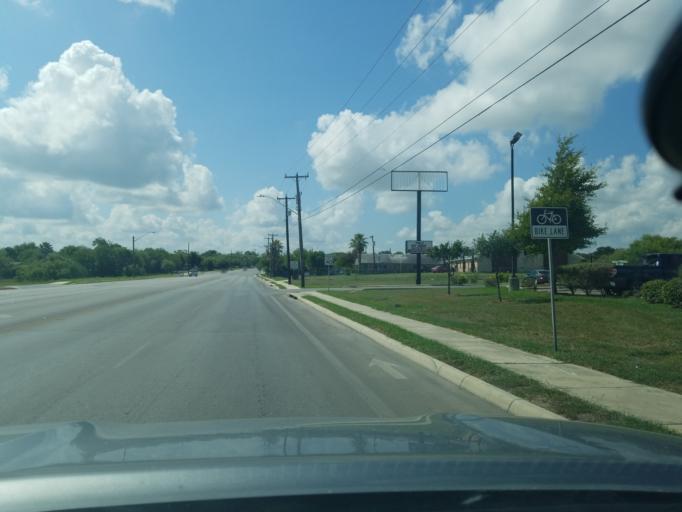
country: US
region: Texas
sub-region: Bexar County
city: Lackland Air Force Base
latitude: 29.3300
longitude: -98.5332
